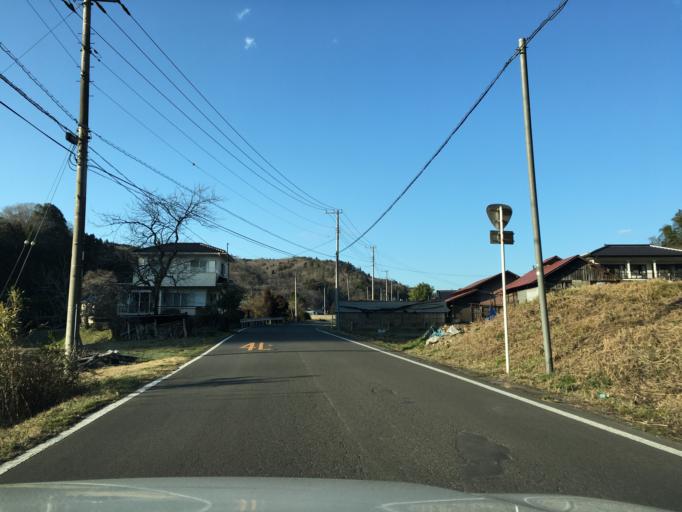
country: JP
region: Tochigi
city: Karasuyama
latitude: 36.7611
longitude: 140.2025
